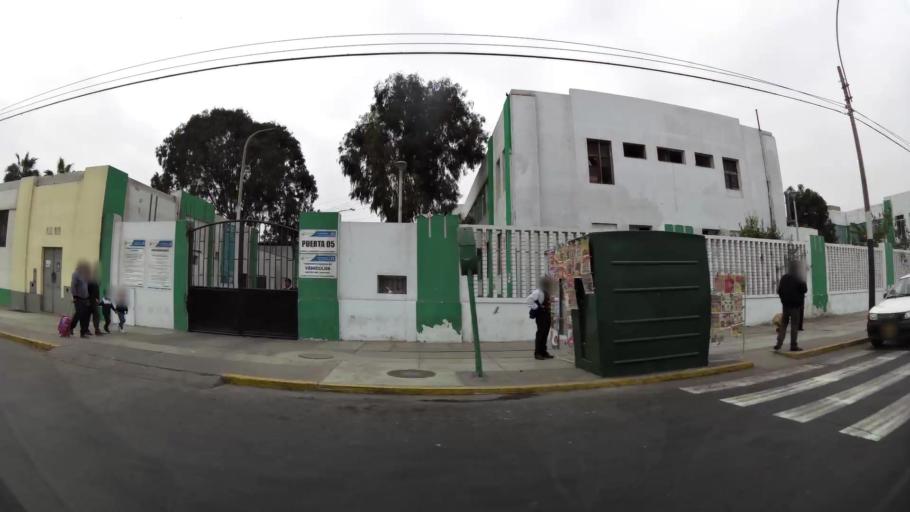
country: PE
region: Callao
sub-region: Callao
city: Callao
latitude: -12.0642
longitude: -77.1250
